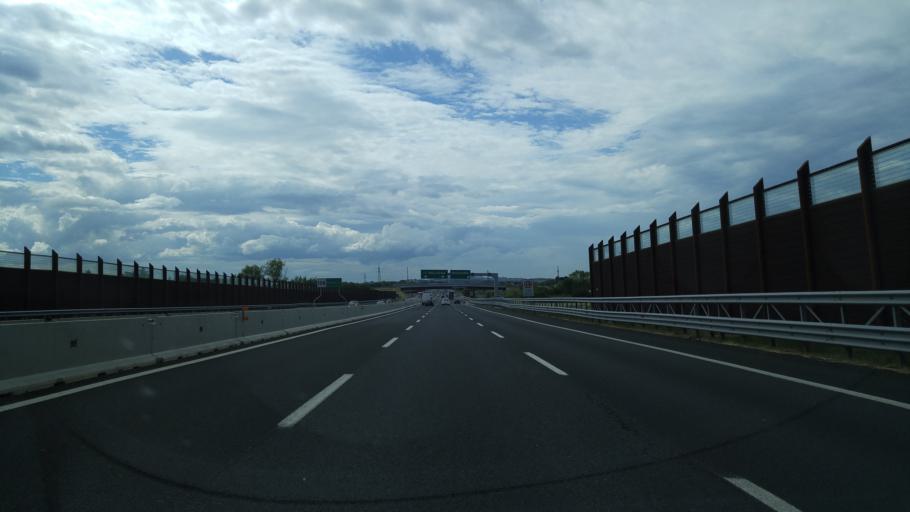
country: IT
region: Emilia-Romagna
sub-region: Provincia di Rimini
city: Riccione
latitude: 43.9833
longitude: 12.6462
